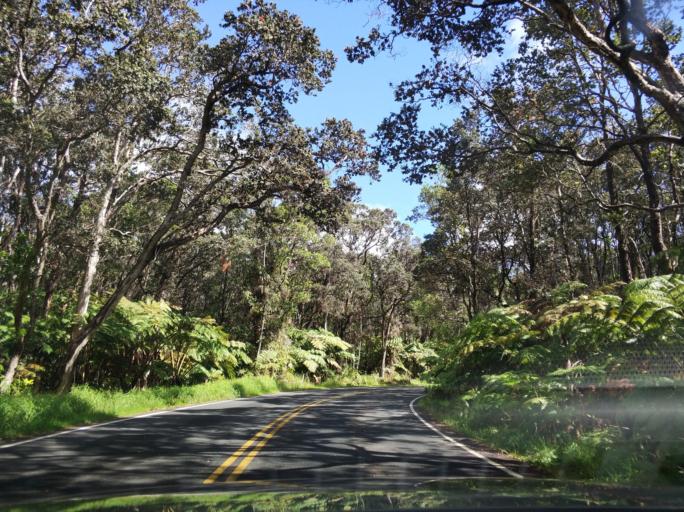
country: US
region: Hawaii
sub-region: Hawaii County
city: Volcano
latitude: 19.4161
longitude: -155.2414
